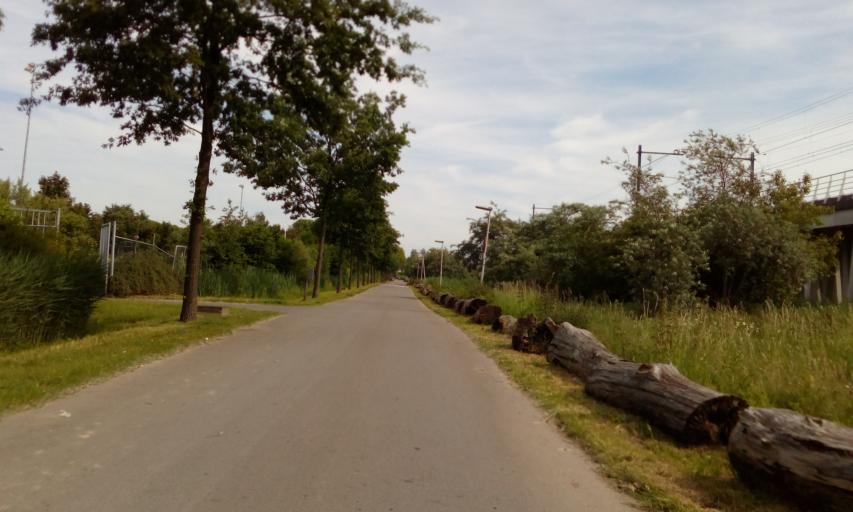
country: NL
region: South Holland
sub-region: Gemeente Rotterdam
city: Delfshaven
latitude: 51.9301
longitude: 4.4483
